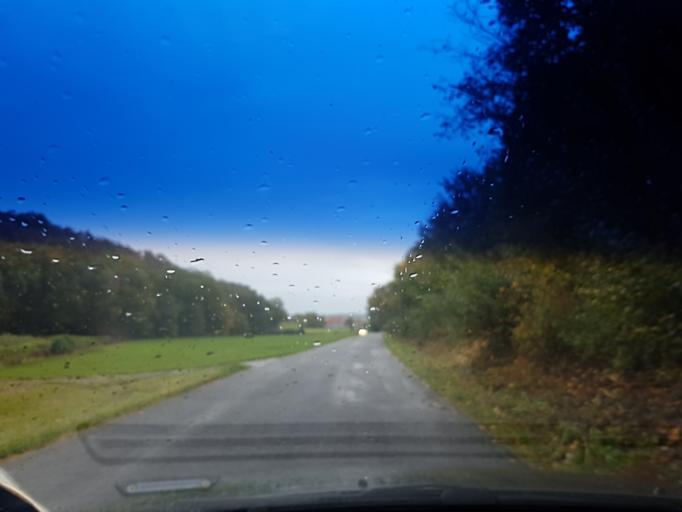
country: DE
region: Bavaria
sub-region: Regierungsbezirk Mittelfranken
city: Wachenroth
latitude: 49.7575
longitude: 10.6943
